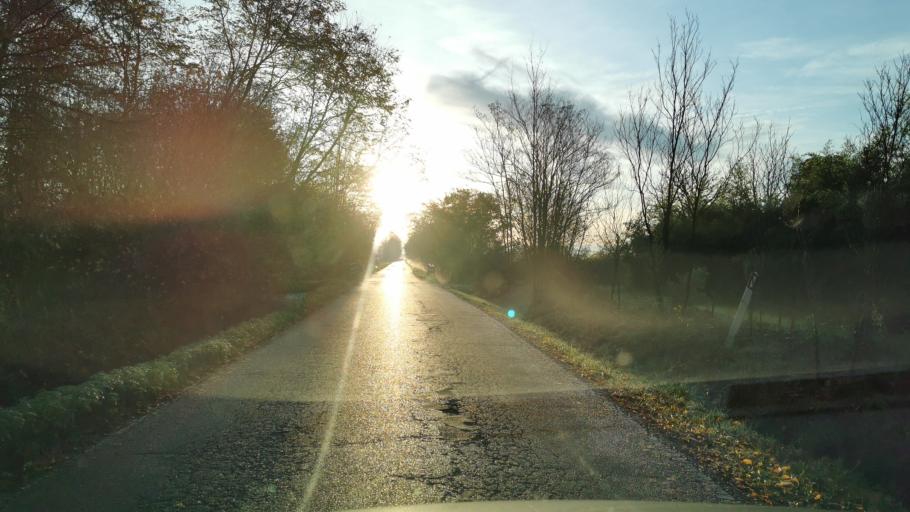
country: IT
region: Piedmont
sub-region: Provincia di Torino
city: San Francesco al Campo
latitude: 45.2065
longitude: 7.6629
